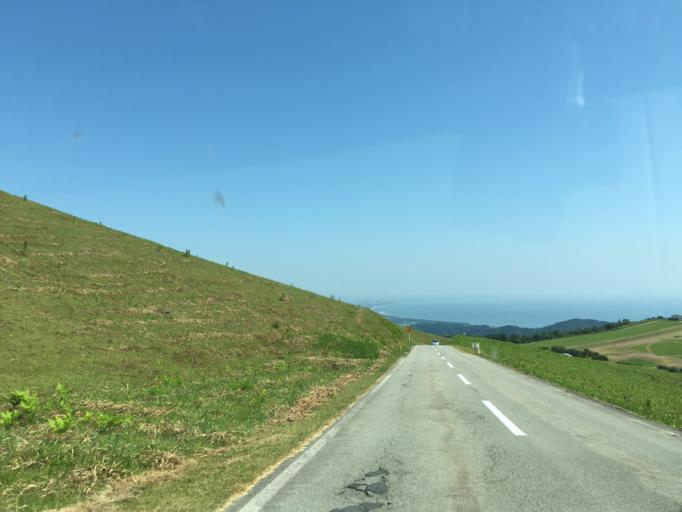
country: JP
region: Akita
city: Tenno
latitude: 39.9299
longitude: 139.8729
